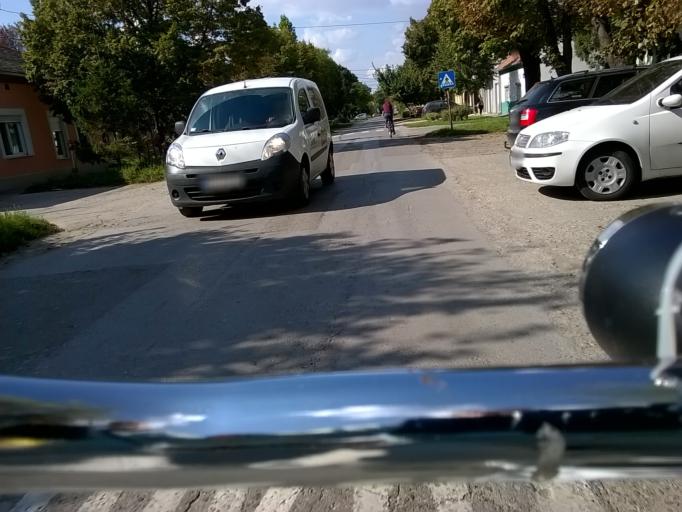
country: RS
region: Autonomna Pokrajina Vojvodina
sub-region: Juznobanatski Okrug
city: Pancevo
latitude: 44.8770
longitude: 20.6373
